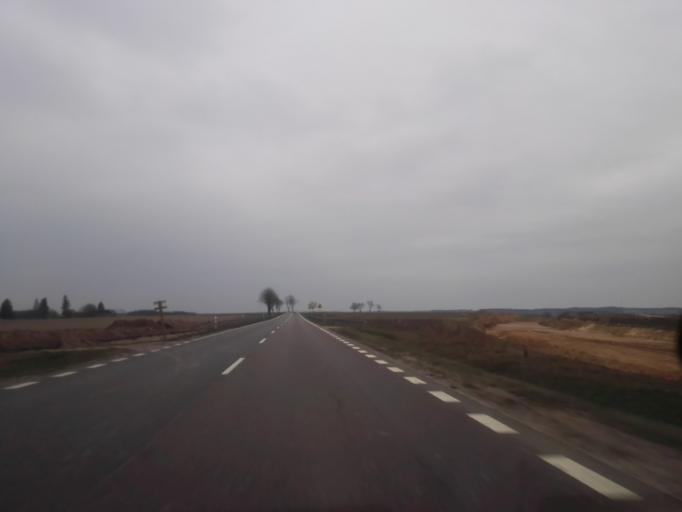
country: PL
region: Podlasie
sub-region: Powiat grajewski
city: Szczuczyn
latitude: 53.5766
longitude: 22.3140
